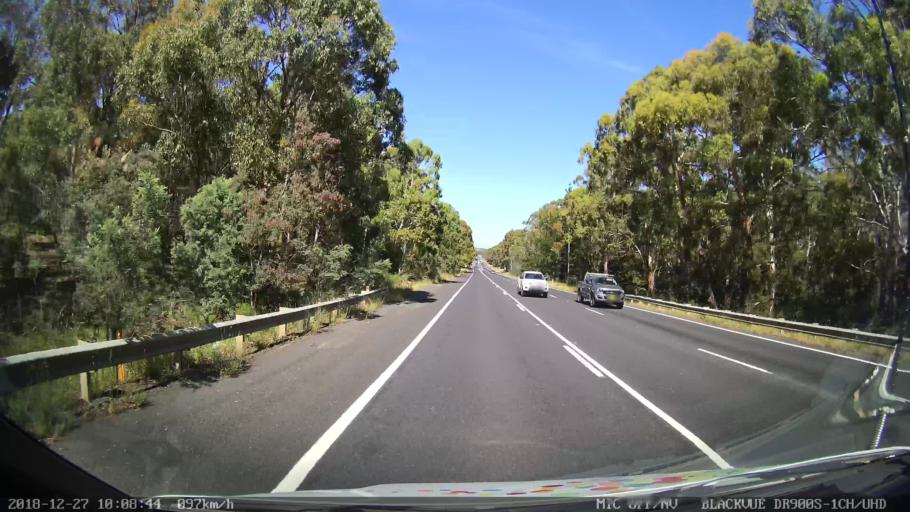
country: AU
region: New South Wales
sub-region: Lithgow
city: Portland
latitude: -33.4489
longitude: 149.8209
